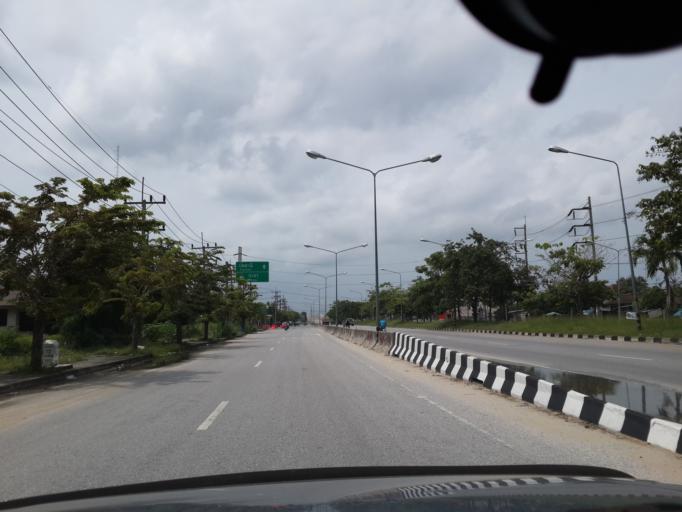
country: TH
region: Pattani
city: Pattani
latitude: 6.8514
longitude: 101.2559
